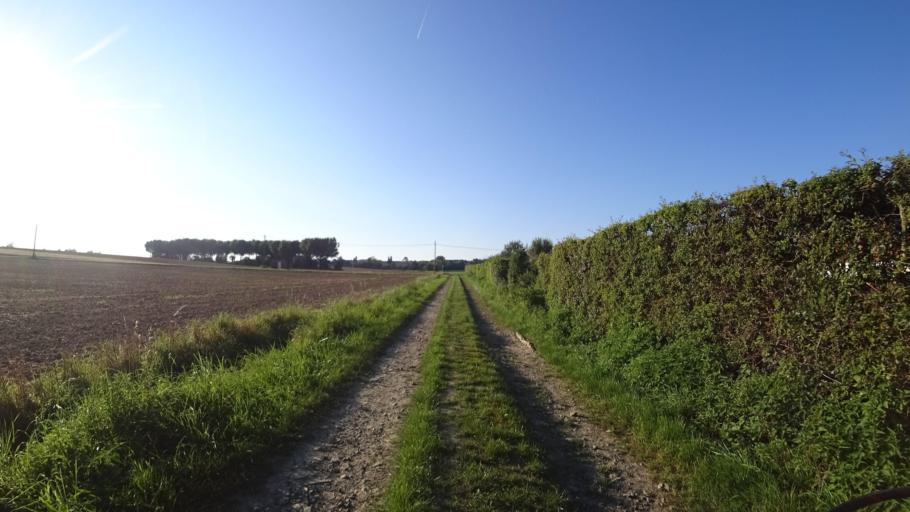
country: BE
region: Wallonia
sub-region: Province du Brabant Wallon
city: Perwez
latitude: 50.5986
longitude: 4.7572
